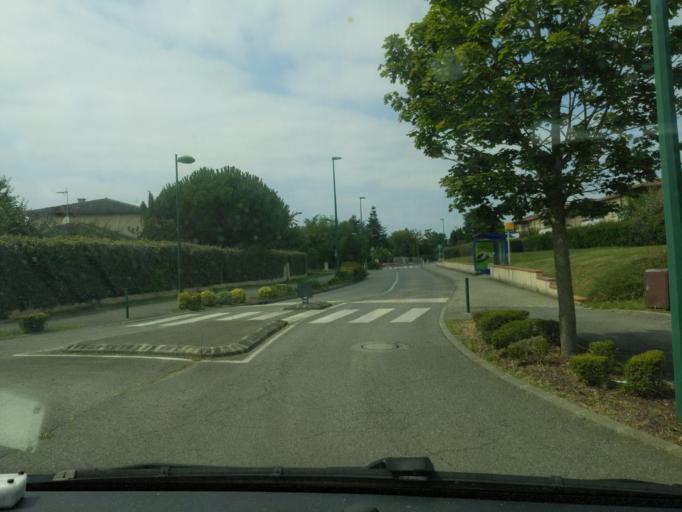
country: FR
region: Midi-Pyrenees
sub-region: Departement de la Haute-Garonne
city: Labege
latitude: 43.5364
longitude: 1.5348
